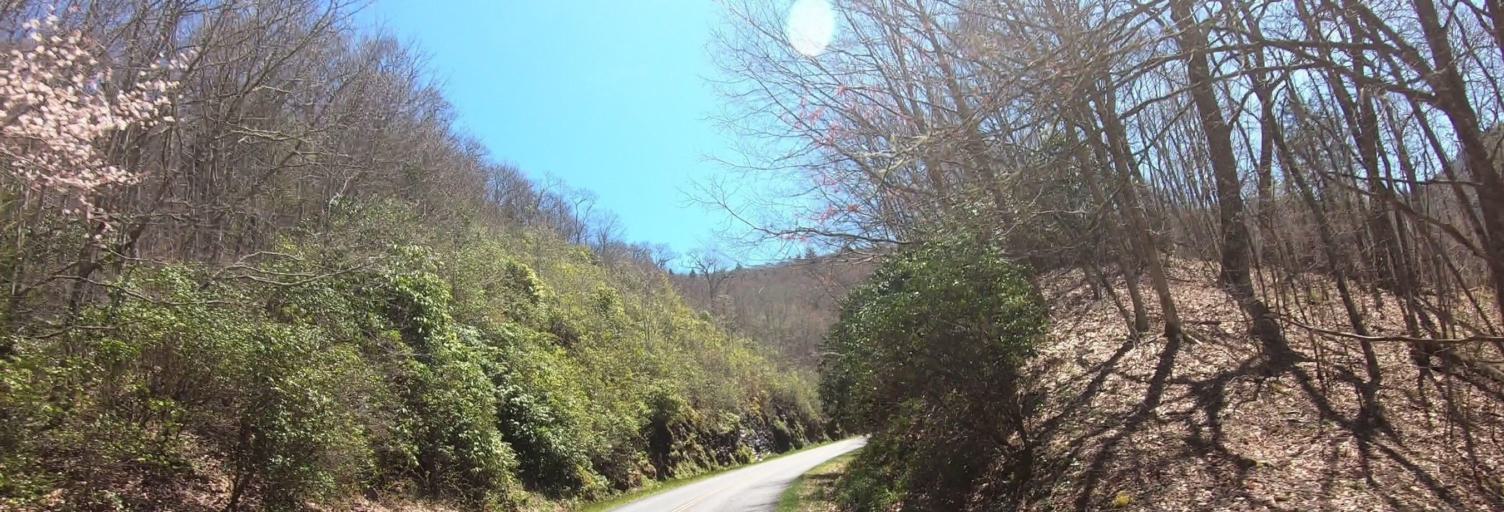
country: US
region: North Carolina
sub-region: Haywood County
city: Maggie Valley
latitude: 35.4777
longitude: -83.1458
